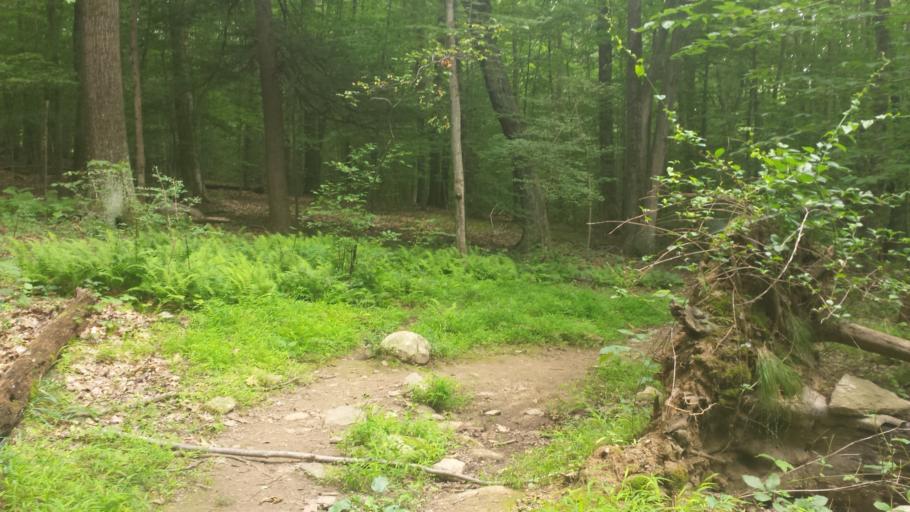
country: US
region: New York
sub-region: Westchester County
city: Yorktown Heights
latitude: 41.2237
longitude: -73.7828
